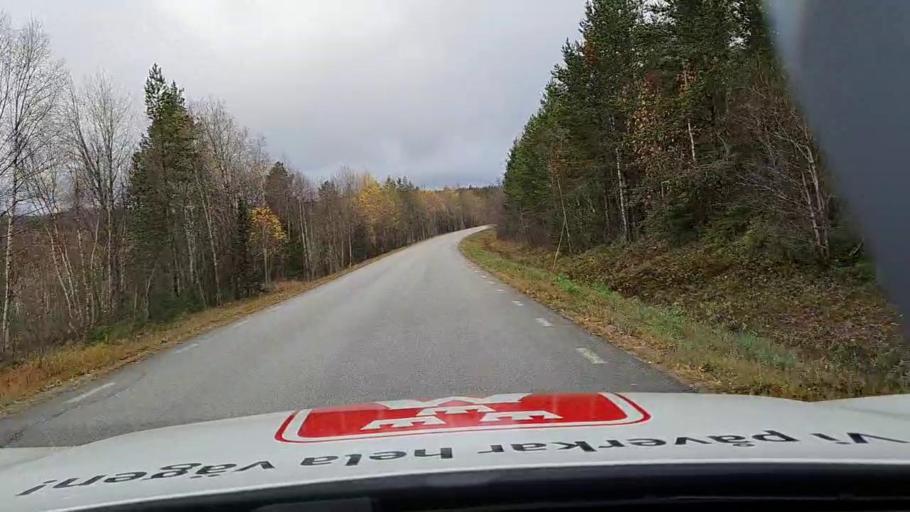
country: SE
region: Jaemtland
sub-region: Bergs Kommun
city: Hoverberg
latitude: 63.0342
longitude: 14.0440
